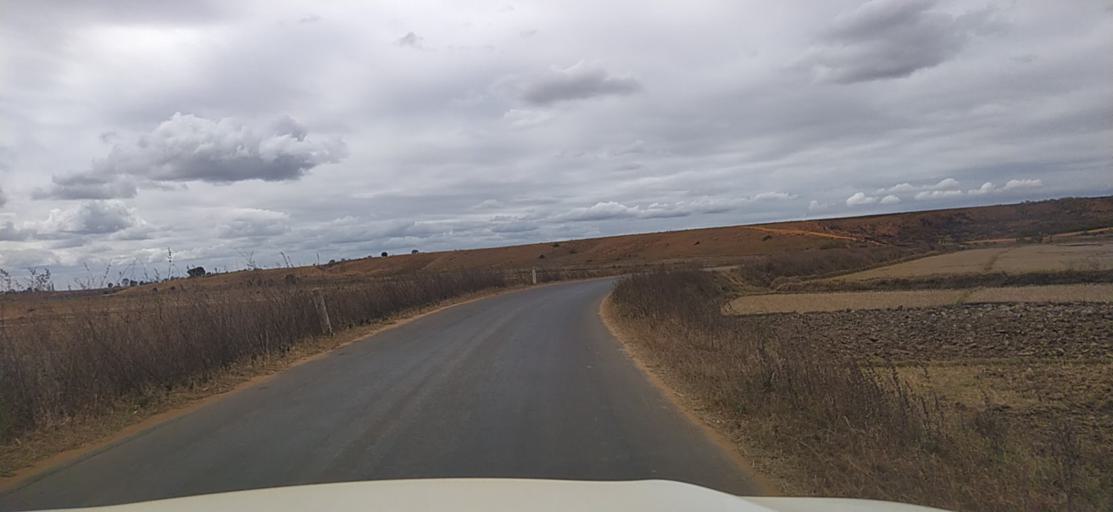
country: MG
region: Alaotra Mangoro
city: Ambatondrazaka
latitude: -17.9154
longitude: 48.2587
